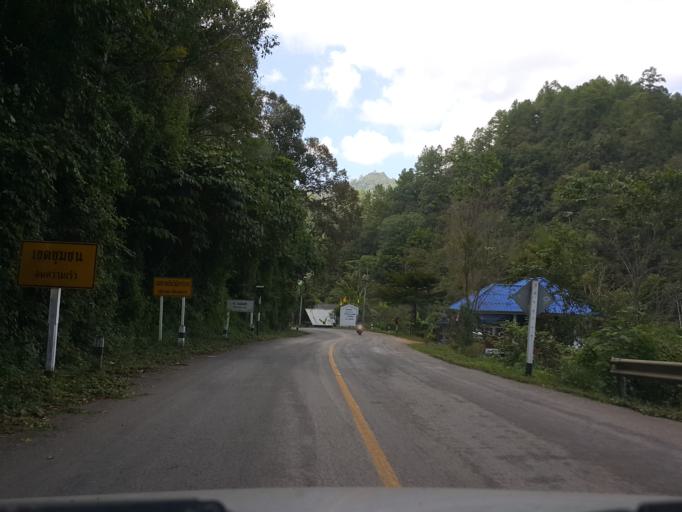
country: TH
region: Mae Hong Son
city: Mae Hi
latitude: 19.2430
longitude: 98.6566
